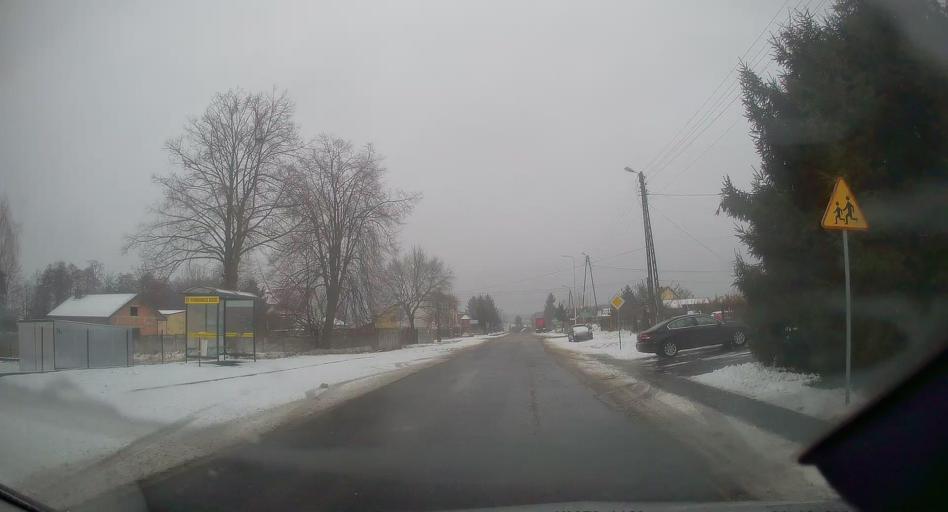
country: PL
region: Lodz Voivodeship
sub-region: Powiat rawski
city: Rawa Mazowiecka
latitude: 51.7066
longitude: 20.2146
